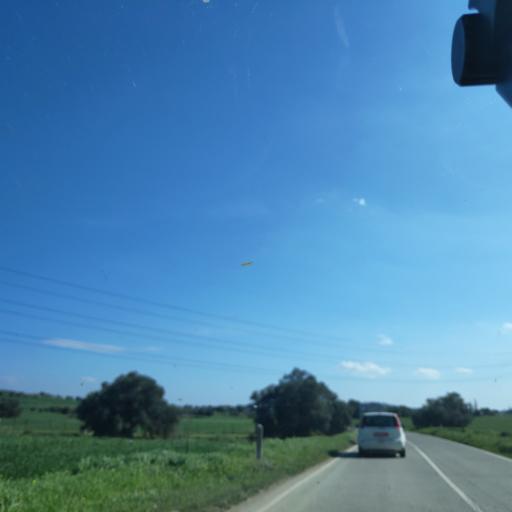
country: CY
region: Lefkosia
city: Tseri
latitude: 35.0193
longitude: 33.3323
